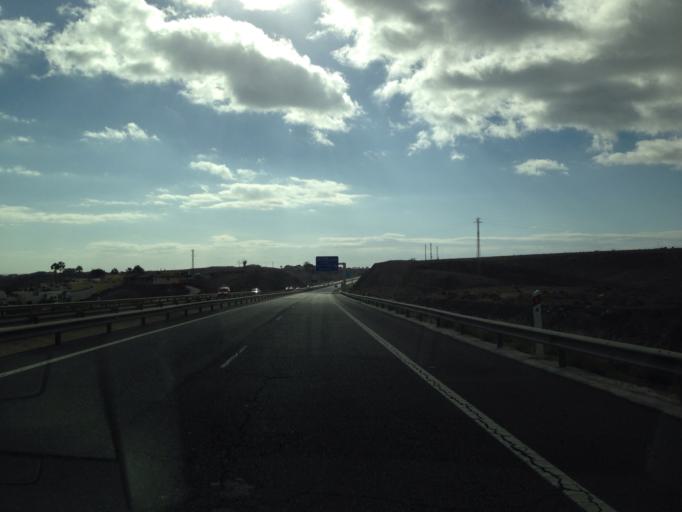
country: ES
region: Canary Islands
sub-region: Provincia de Las Palmas
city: Maspalomas
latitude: 27.7629
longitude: -15.6053
